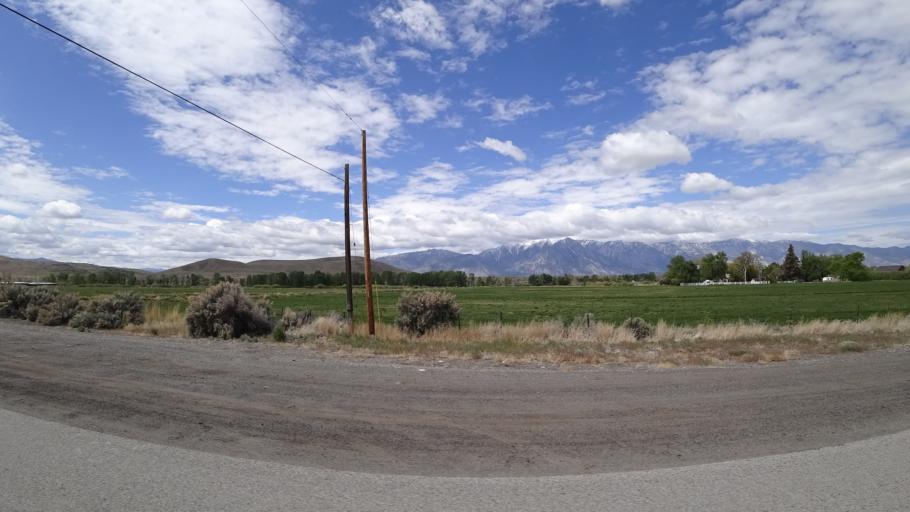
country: US
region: Nevada
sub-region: Douglas County
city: Gardnerville Ranchos
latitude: 38.8917
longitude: -119.6994
